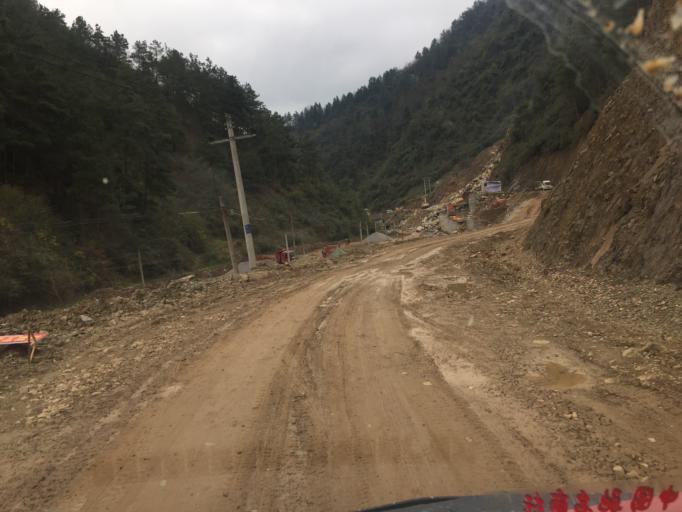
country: CN
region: Guizhou Sheng
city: Fuxing
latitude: 28.0729
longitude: 107.9065
